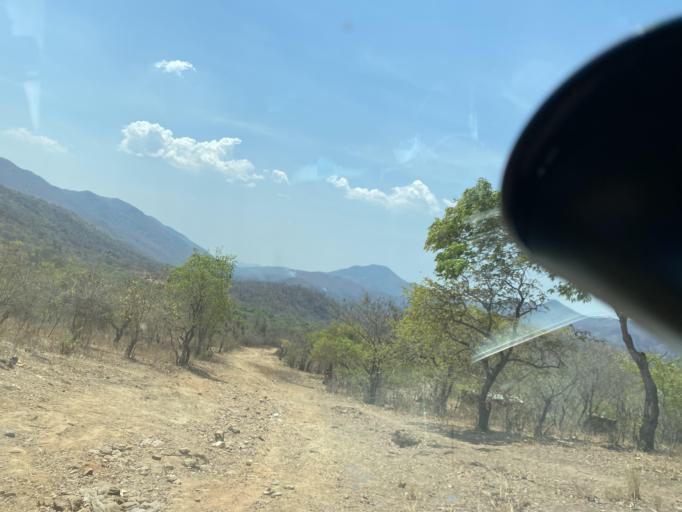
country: ZM
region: Lusaka
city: Kafue
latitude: -15.7954
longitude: 28.4563
